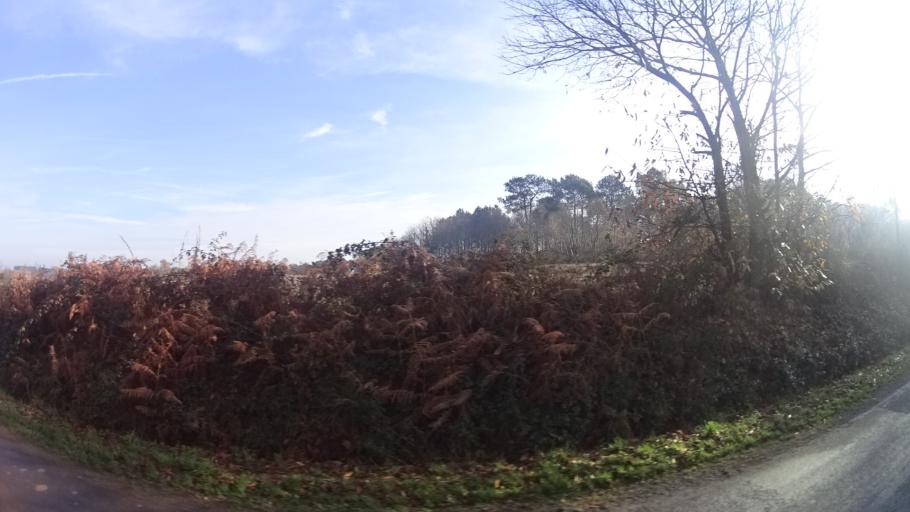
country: FR
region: Brittany
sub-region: Departement du Morbihan
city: Allaire
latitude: 47.6057
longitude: -2.1477
